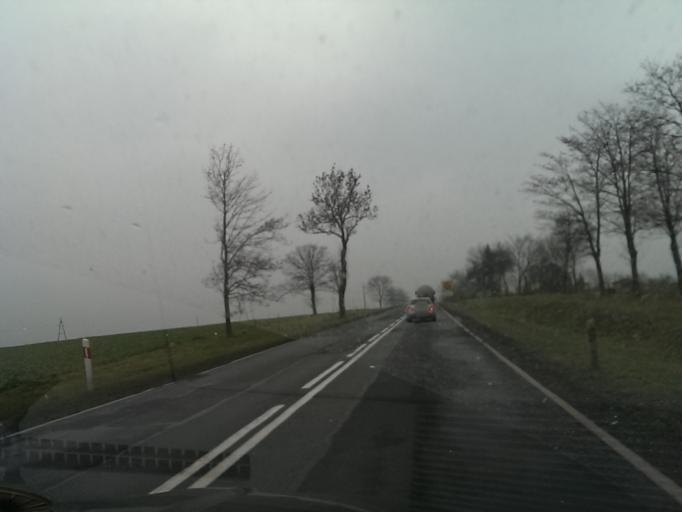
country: PL
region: Kujawsko-Pomorskie
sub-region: Powiat nakielski
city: Slesin
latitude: 53.1651
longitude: 17.6594
